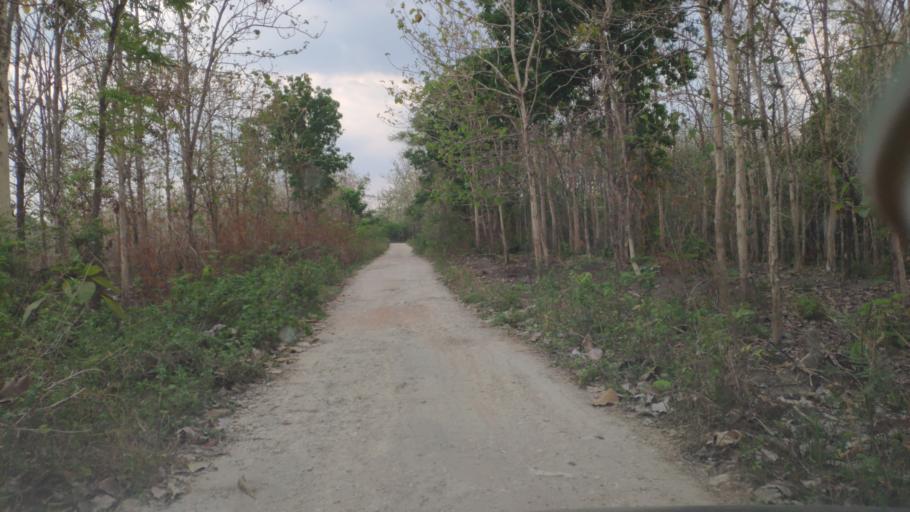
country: ID
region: Central Java
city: Randublatung
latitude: -7.2774
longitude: 111.2873
